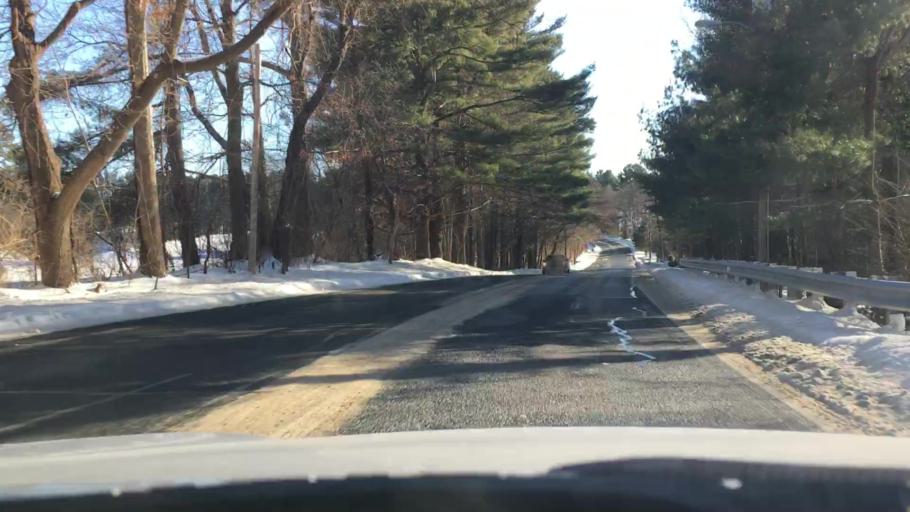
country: US
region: Massachusetts
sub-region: Hampden County
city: Longmeadow
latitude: 42.0453
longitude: -72.5723
